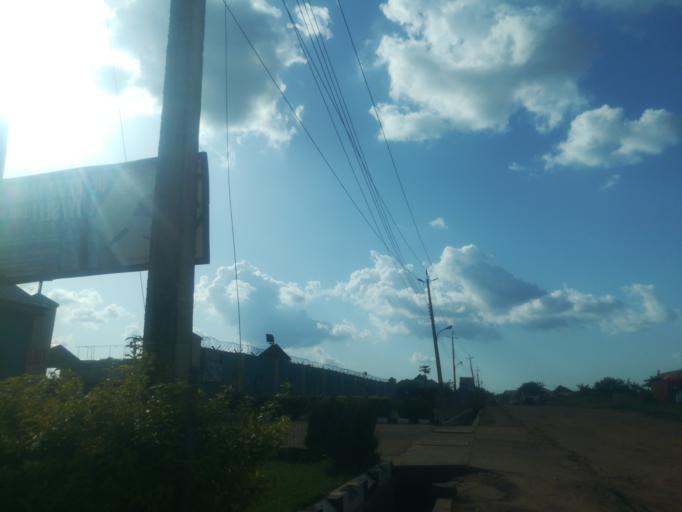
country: NG
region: Oyo
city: Ibadan
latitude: 7.4335
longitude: 3.9774
